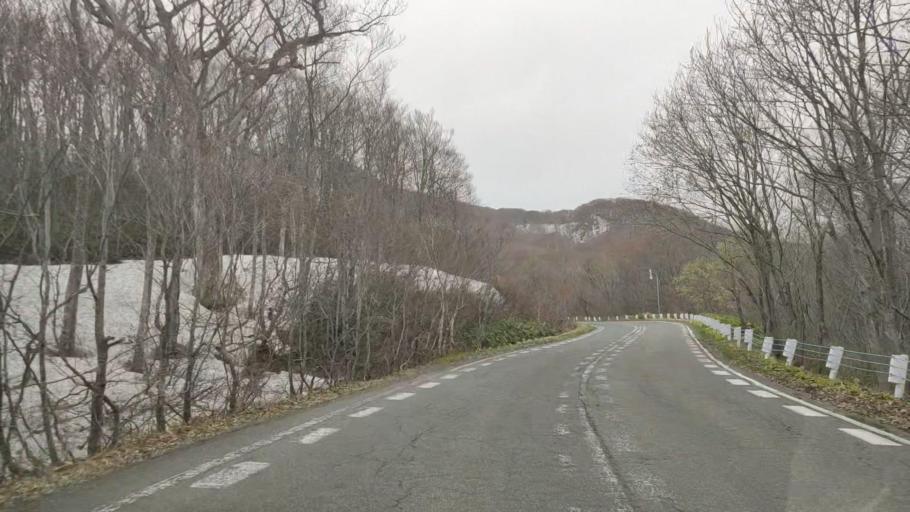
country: JP
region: Aomori
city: Aomori Shi
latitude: 40.6566
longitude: 140.9556
